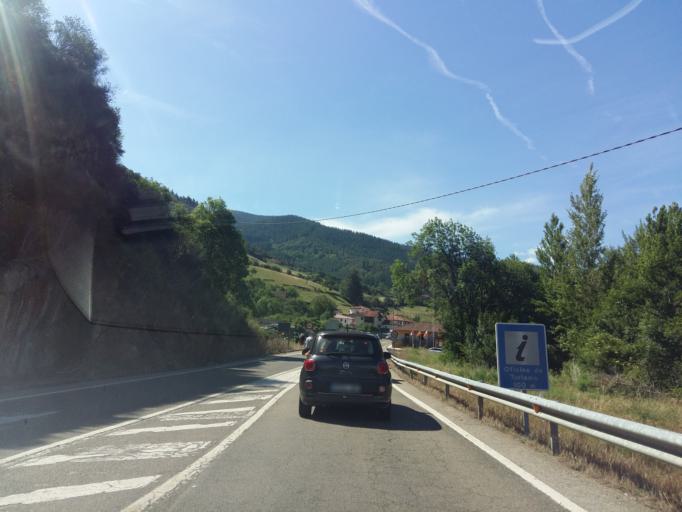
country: ES
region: Cantabria
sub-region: Provincia de Cantabria
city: Potes
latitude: 43.1787
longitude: -4.6008
